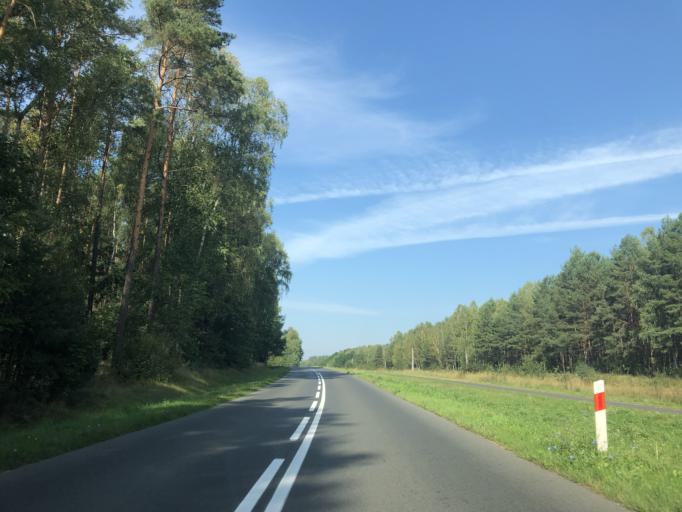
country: PL
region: Greater Poland Voivodeship
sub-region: Powiat pilski
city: Kaczory
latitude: 53.1262
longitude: 16.8123
